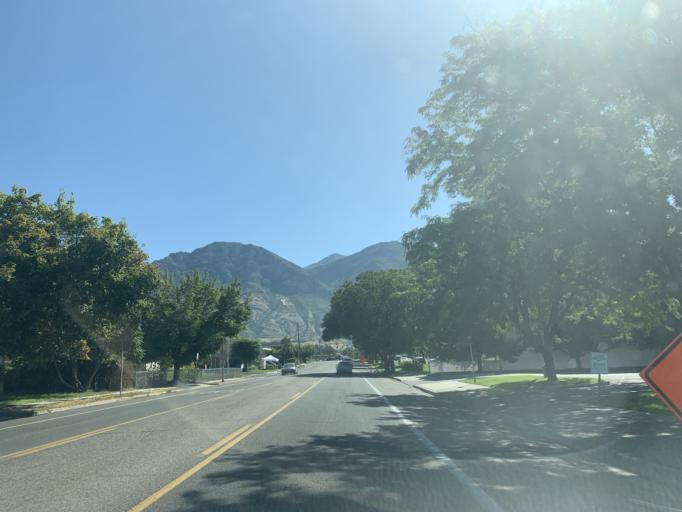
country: US
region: Utah
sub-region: Utah County
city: Provo
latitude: 40.2443
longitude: -111.6702
